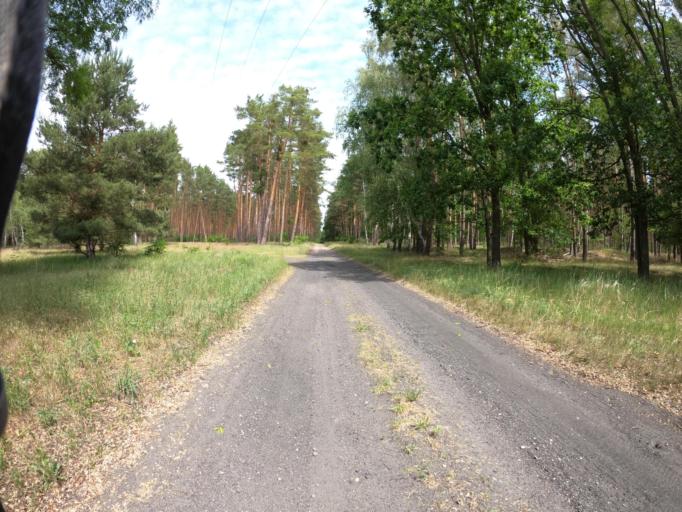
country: DE
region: Brandenburg
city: Zechin
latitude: 52.6809
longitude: 14.4893
